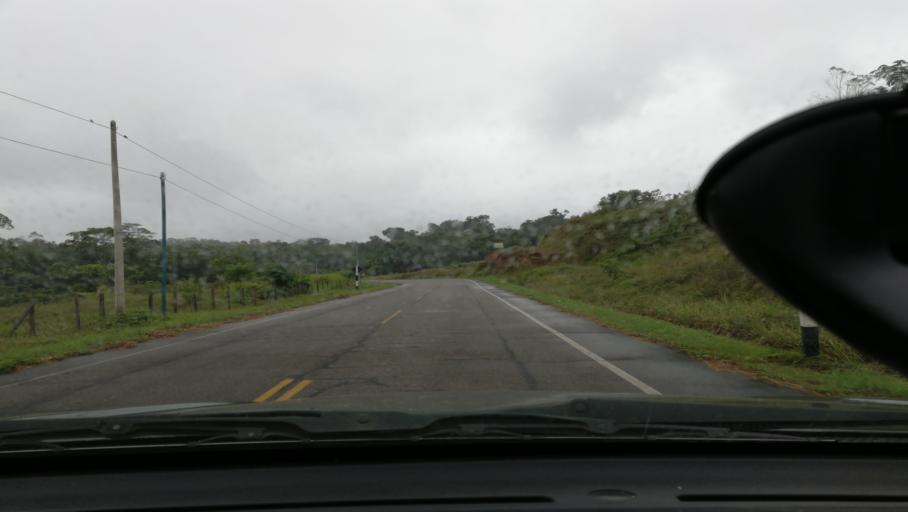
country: PE
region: Loreto
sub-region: Provincia de Loreto
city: Nauta
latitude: -4.4383
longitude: -73.5874
